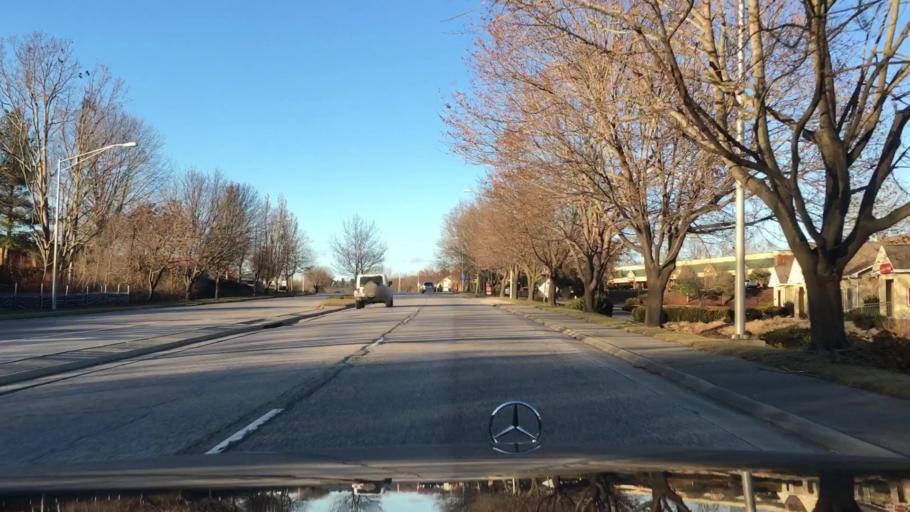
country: US
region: Virginia
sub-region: Montgomery County
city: Blacksburg
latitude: 37.2054
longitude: -80.3988
